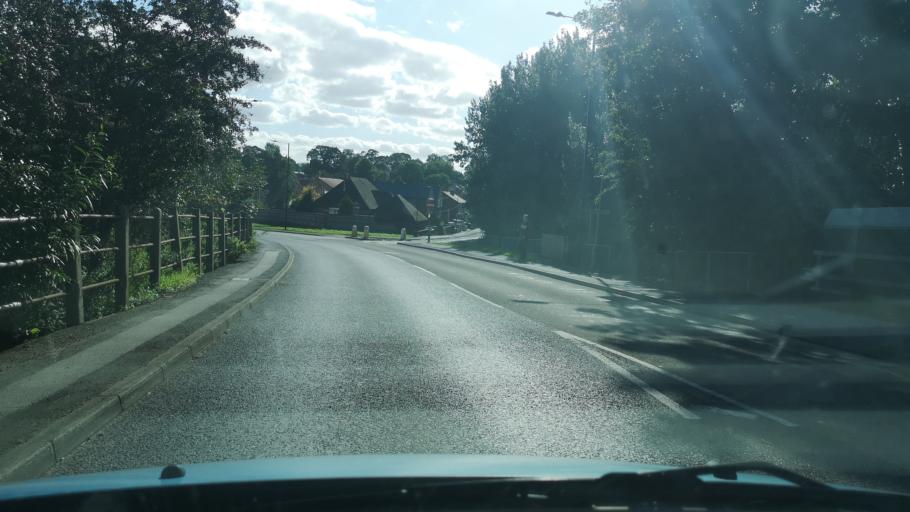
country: GB
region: England
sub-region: Doncaster
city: Carcroft
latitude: 53.5728
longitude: -1.1813
